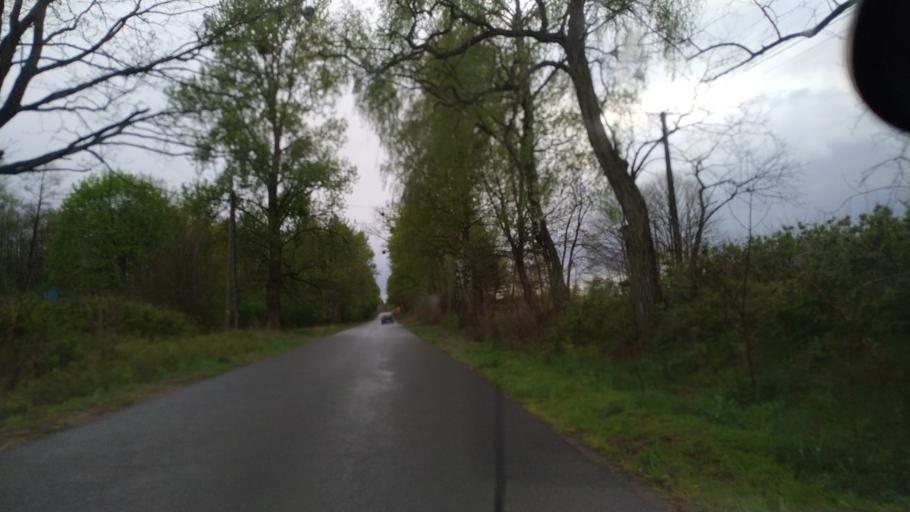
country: PL
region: Pomeranian Voivodeship
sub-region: Powiat starogardzki
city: Osiek
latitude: 53.6423
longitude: 18.4854
